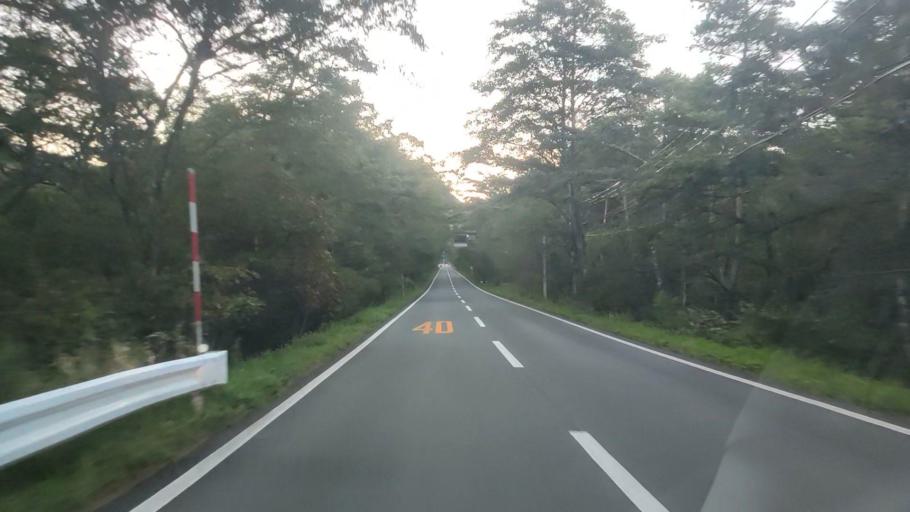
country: JP
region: Nagano
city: Komoro
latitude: 36.4001
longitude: 138.5729
